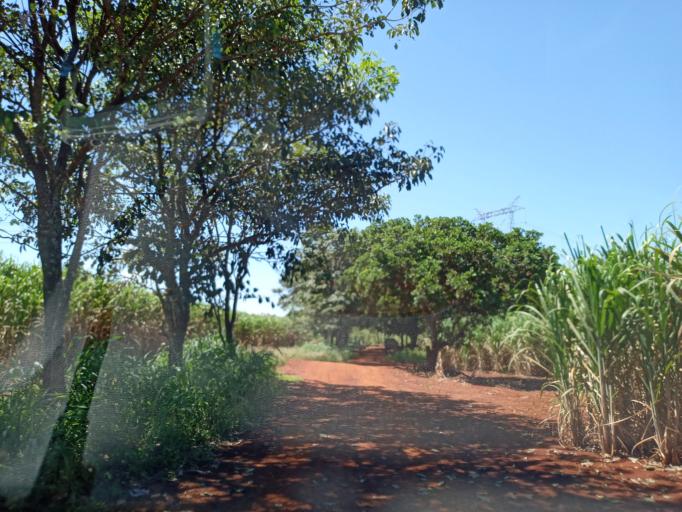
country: BR
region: Goias
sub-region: Itumbiara
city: Itumbiara
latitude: -18.4406
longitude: -49.1325
